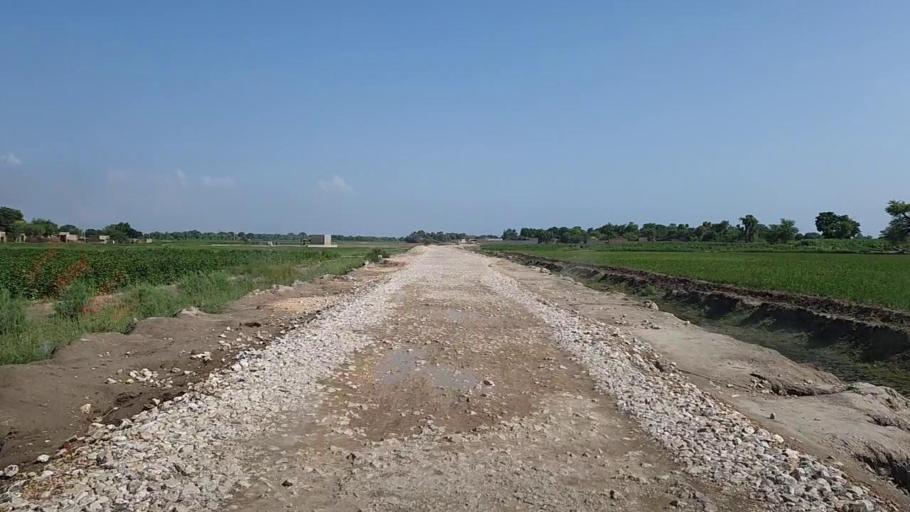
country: PK
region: Sindh
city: Bhiria
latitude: 26.8734
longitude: 68.2322
